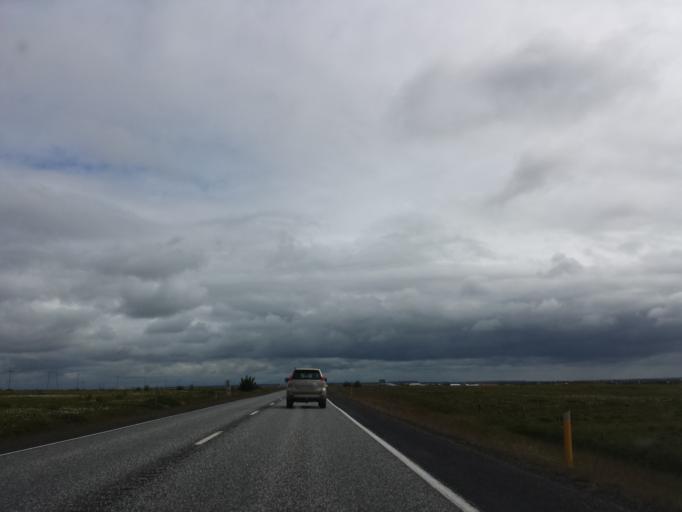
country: IS
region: South
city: Selfoss
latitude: 63.9542
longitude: -21.0402
